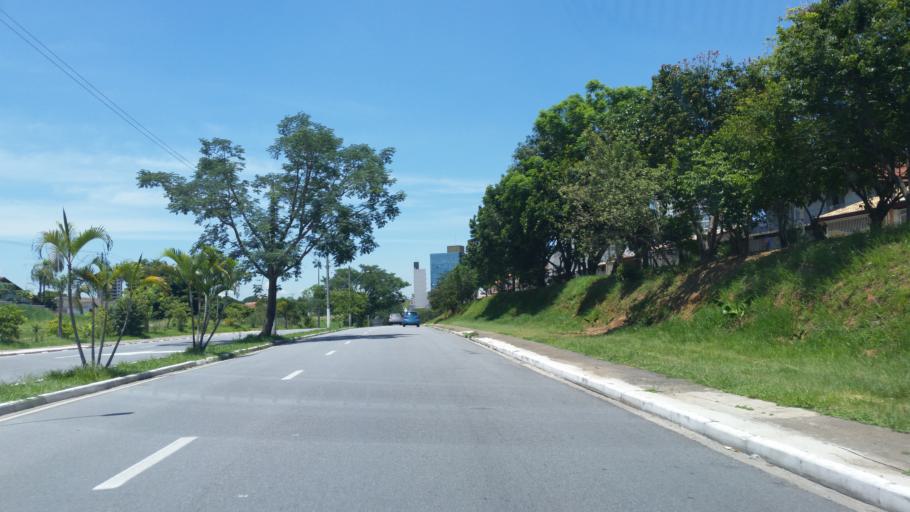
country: BR
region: Sao Paulo
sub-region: Taubate
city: Taubate
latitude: -23.0281
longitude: -45.5743
